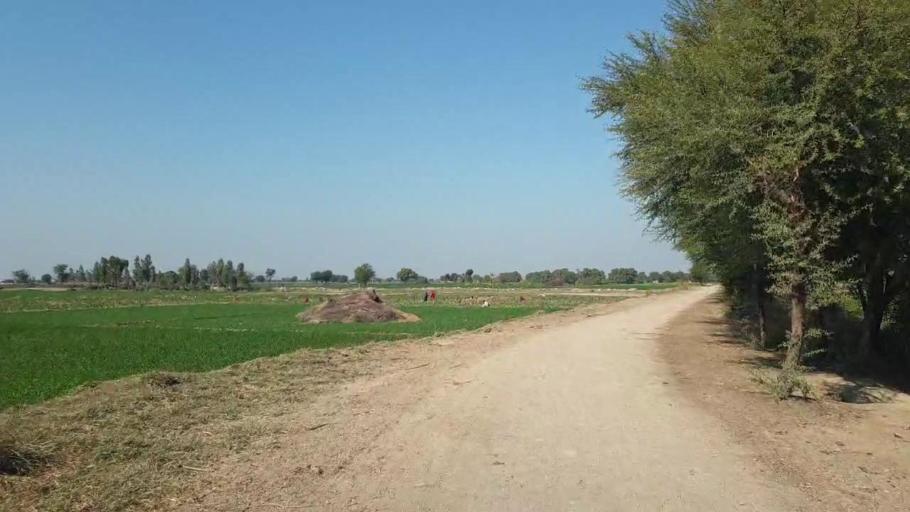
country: PK
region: Sindh
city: Shahdadpur
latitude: 25.9582
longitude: 68.6517
